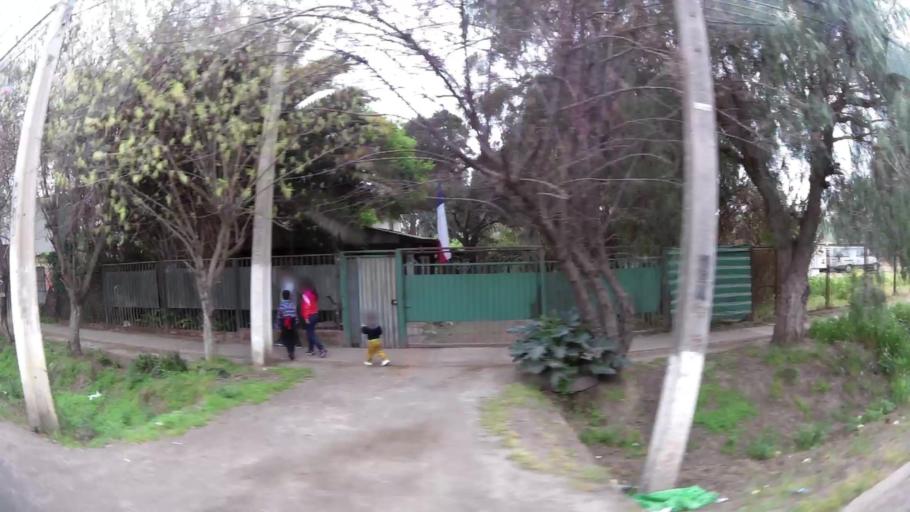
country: CL
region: Santiago Metropolitan
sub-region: Provincia de Chacabuco
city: Lampa
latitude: -33.2374
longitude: -70.8066
